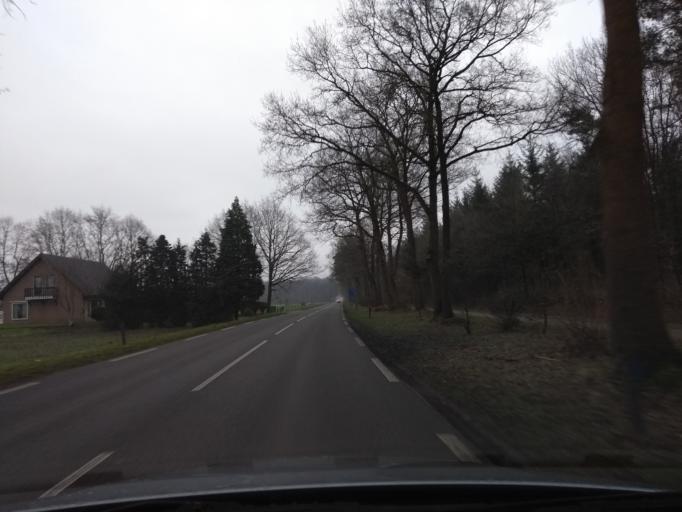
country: NL
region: Overijssel
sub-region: Gemeente Borne
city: Borne
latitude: 52.3143
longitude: 6.6964
